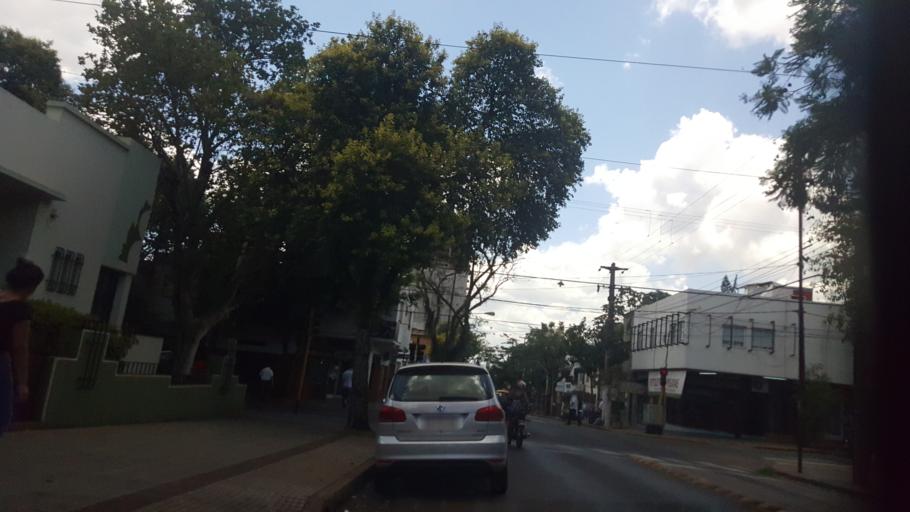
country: AR
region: Misiones
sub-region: Departamento de Capital
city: Posadas
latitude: -27.3651
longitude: -55.8966
